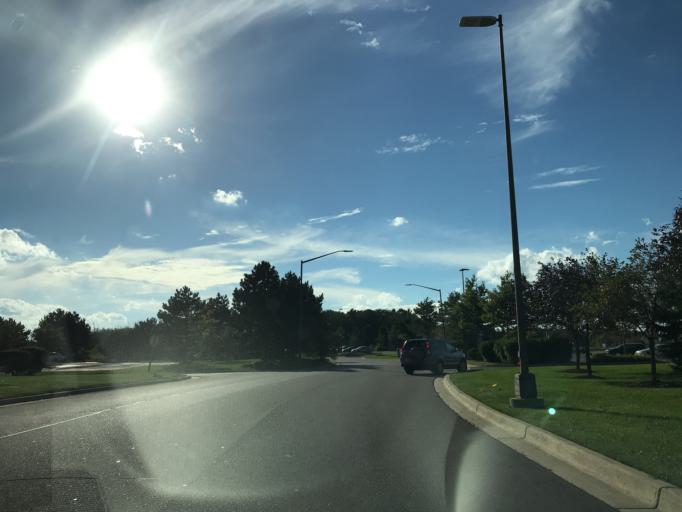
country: US
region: Michigan
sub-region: Oakland County
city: Walled Lake
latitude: 42.5329
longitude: -83.4444
